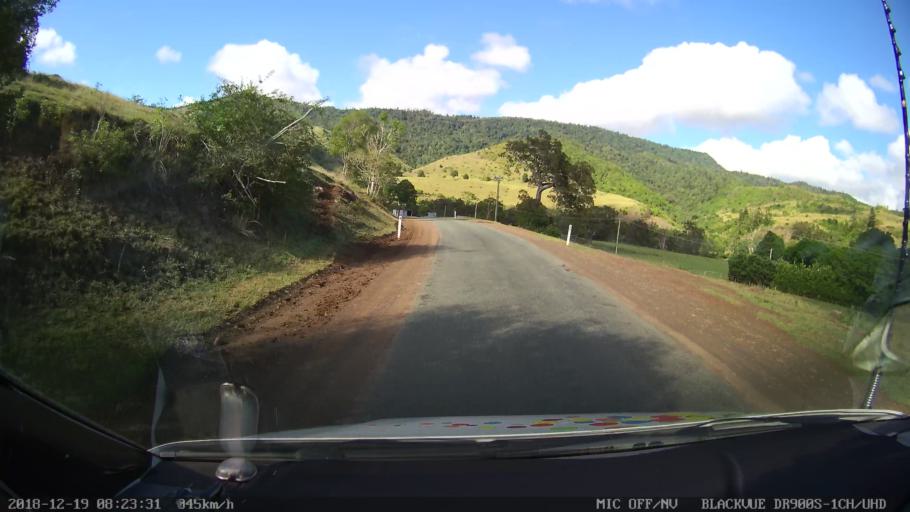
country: AU
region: New South Wales
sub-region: Kyogle
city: Kyogle
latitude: -28.3071
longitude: 152.9082
